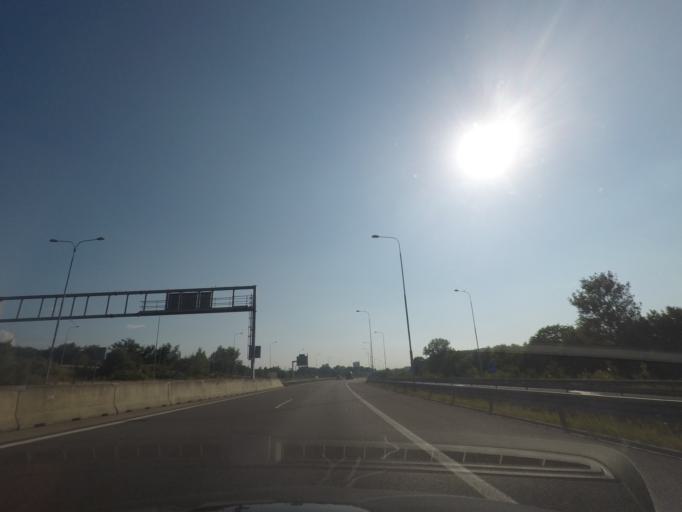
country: CZ
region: Moravskoslezsky
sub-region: Okres Ostrava-Mesto
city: Ostrava
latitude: 49.8752
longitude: 18.2998
